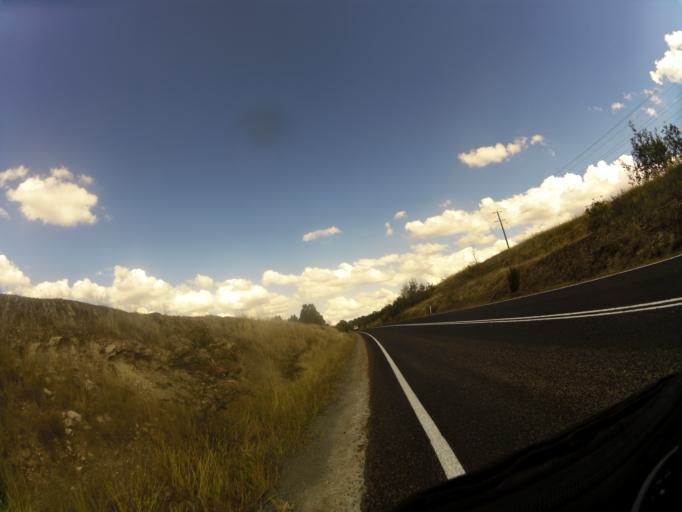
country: AU
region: Victoria
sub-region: Mansfield
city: Mansfield
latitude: -36.9066
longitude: 145.9974
